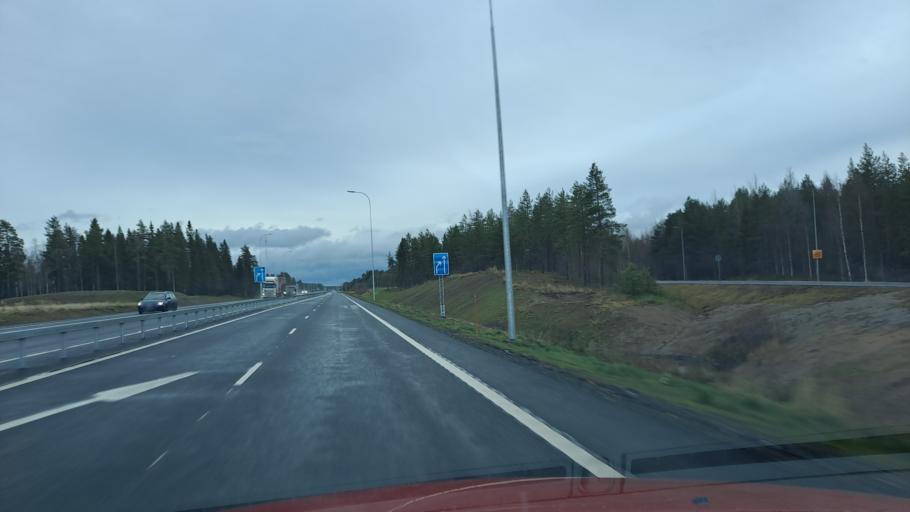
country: FI
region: Northern Ostrobothnia
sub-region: Oulu
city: Haukipudas
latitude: 65.2418
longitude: 25.3847
